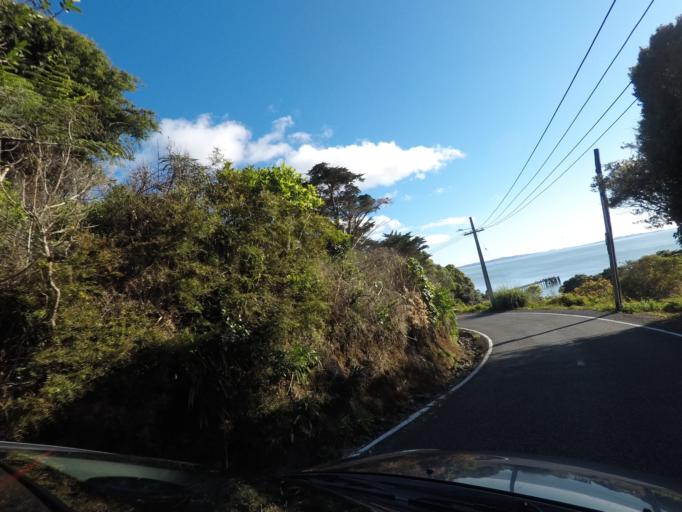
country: NZ
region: Auckland
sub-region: Auckland
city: Titirangi
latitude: -37.0133
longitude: 174.6046
